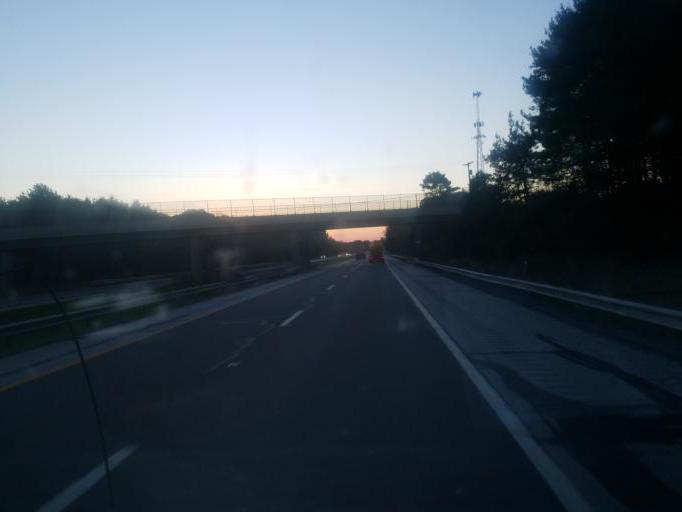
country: US
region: Ohio
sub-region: Mahoning County
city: Canfield
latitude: 41.0319
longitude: -80.7377
